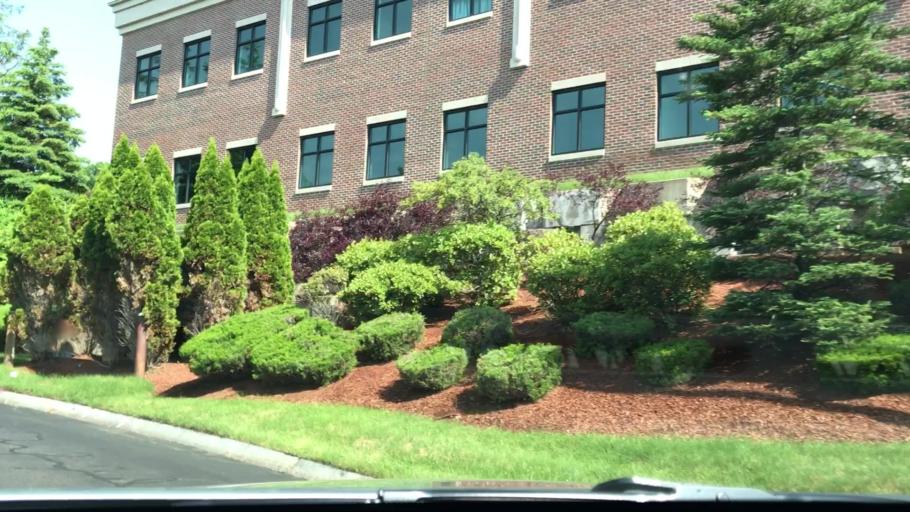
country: US
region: Massachusetts
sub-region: Middlesex County
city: Marlborough
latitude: 42.3200
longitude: -71.5860
